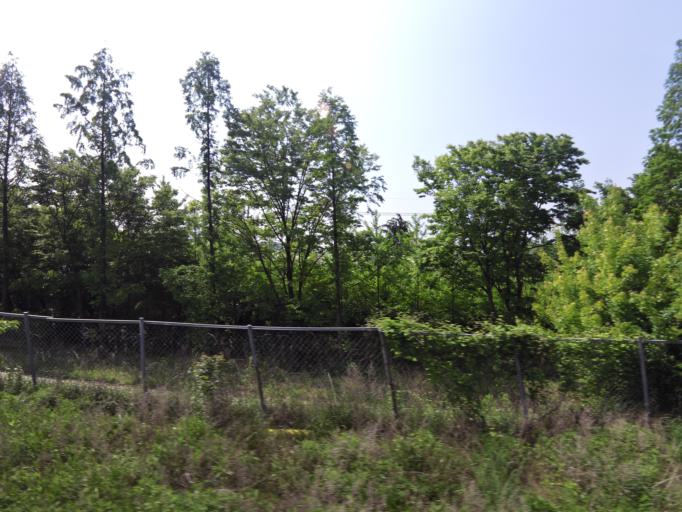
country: KR
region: Daegu
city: Daegu
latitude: 35.8815
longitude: 128.5359
